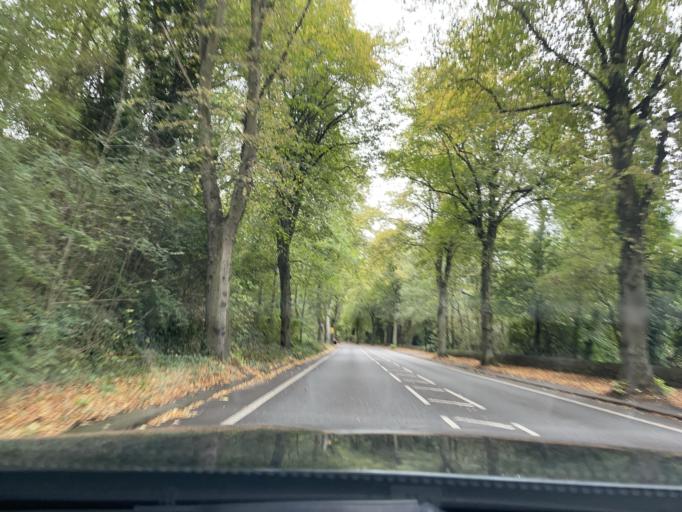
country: GB
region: England
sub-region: Sheffield
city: Oughtibridge
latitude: 53.3946
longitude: -1.5138
